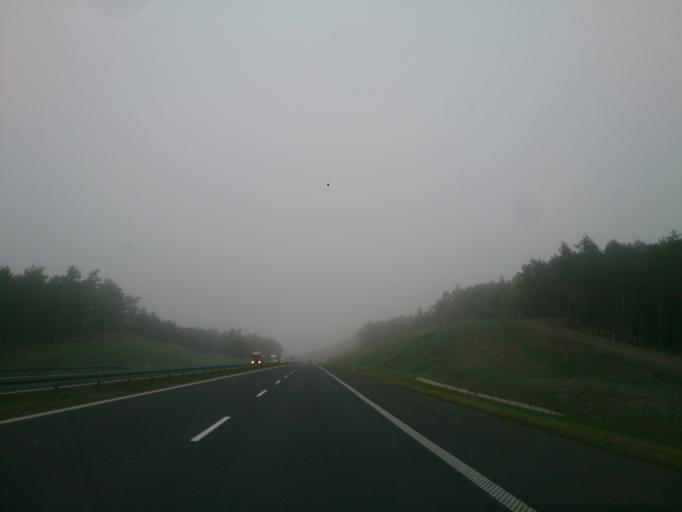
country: PL
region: Kujawsko-Pomorskie
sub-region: Powiat swiecki
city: Warlubie
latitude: 53.4824
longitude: 18.6168
